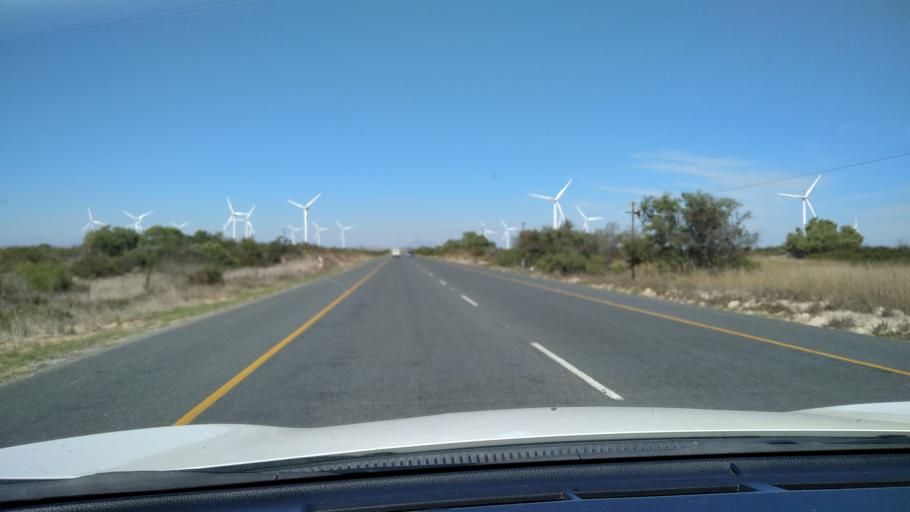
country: ZA
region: Western Cape
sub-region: West Coast District Municipality
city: Moorreesburg
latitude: -33.0763
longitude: 18.3816
